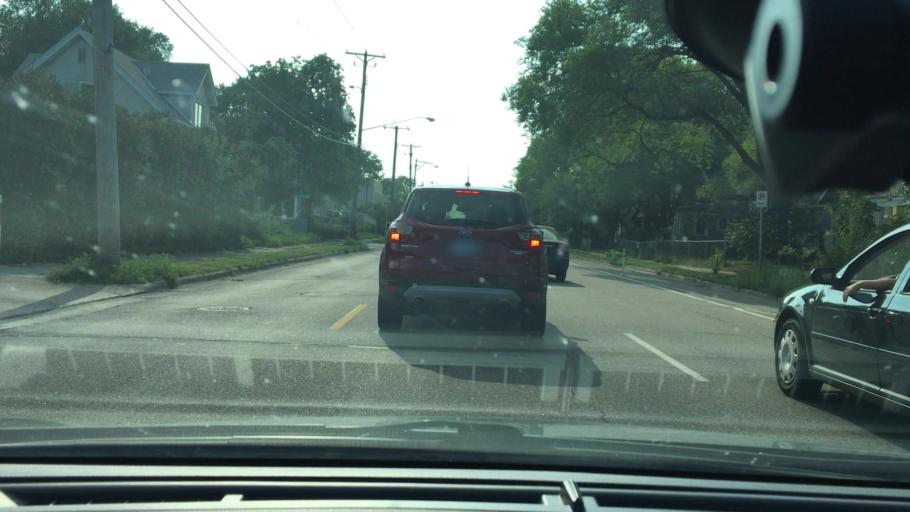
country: US
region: Minnesota
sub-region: Hennepin County
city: Minneapolis
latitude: 44.9556
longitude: -93.2453
